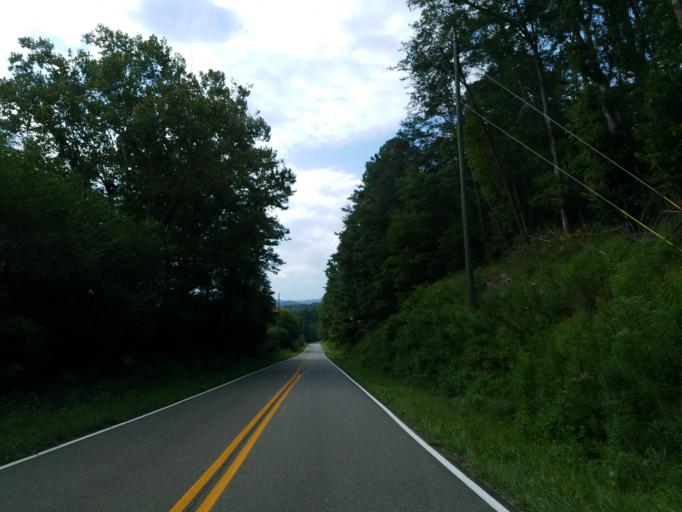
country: US
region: Georgia
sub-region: Gilmer County
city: Ellijay
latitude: 34.7769
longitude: -84.4213
